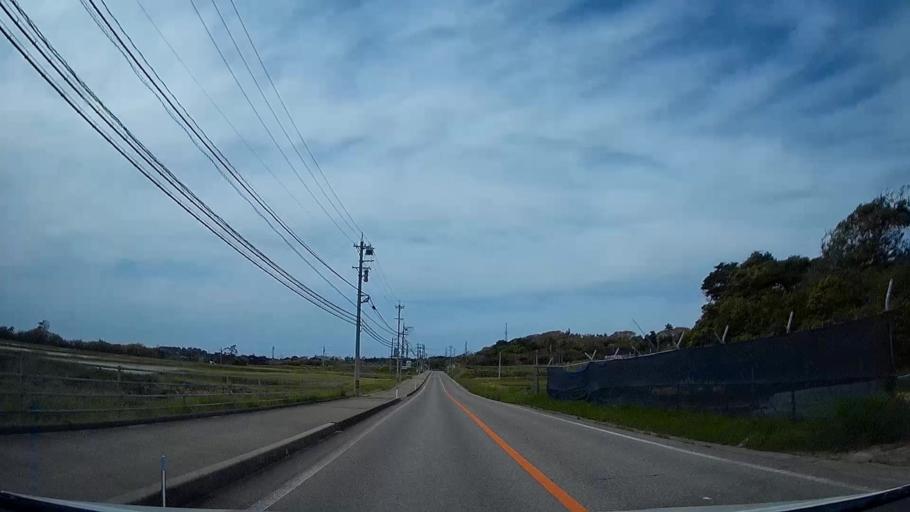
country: JP
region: Ishikawa
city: Hakui
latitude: 37.0462
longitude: 136.7381
